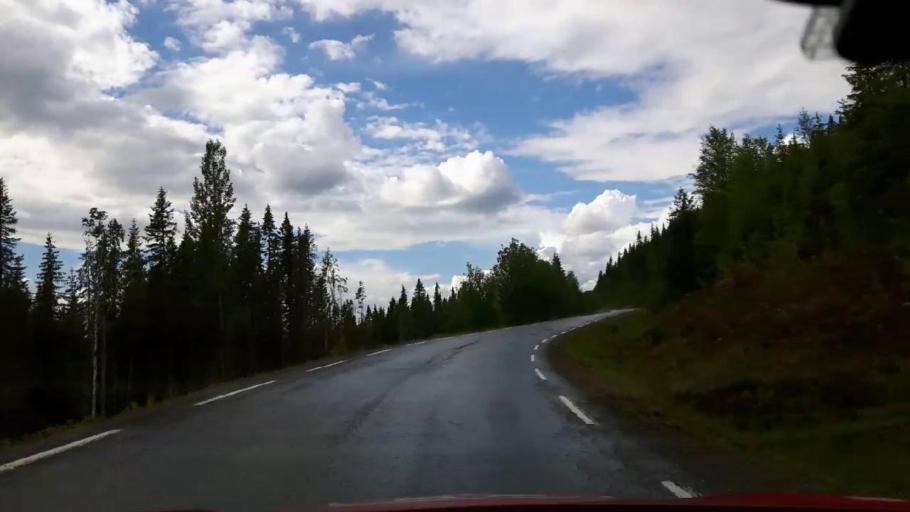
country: NO
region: Nord-Trondelag
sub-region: Lierne
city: Sandvika
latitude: 64.1024
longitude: 14.0009
